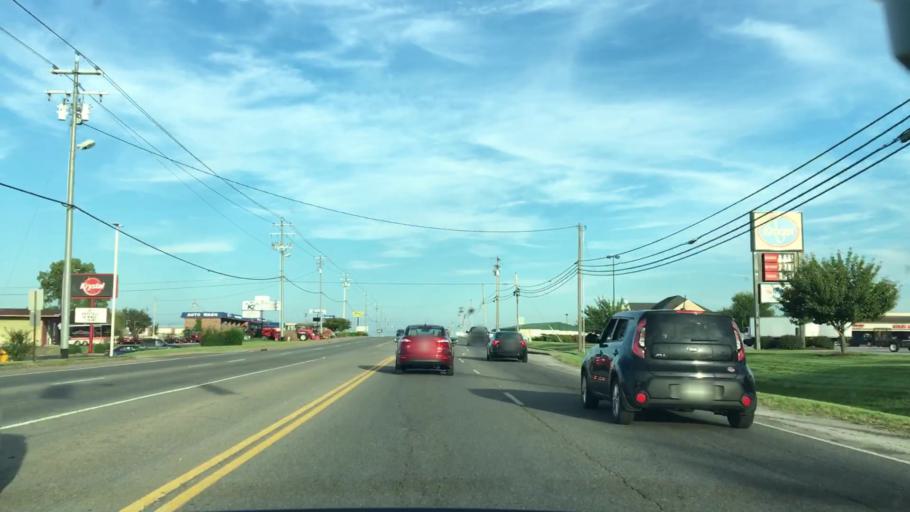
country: US
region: Tennessee
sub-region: Wilson County
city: Lebanon
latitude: 36.2164
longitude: -86.3308
